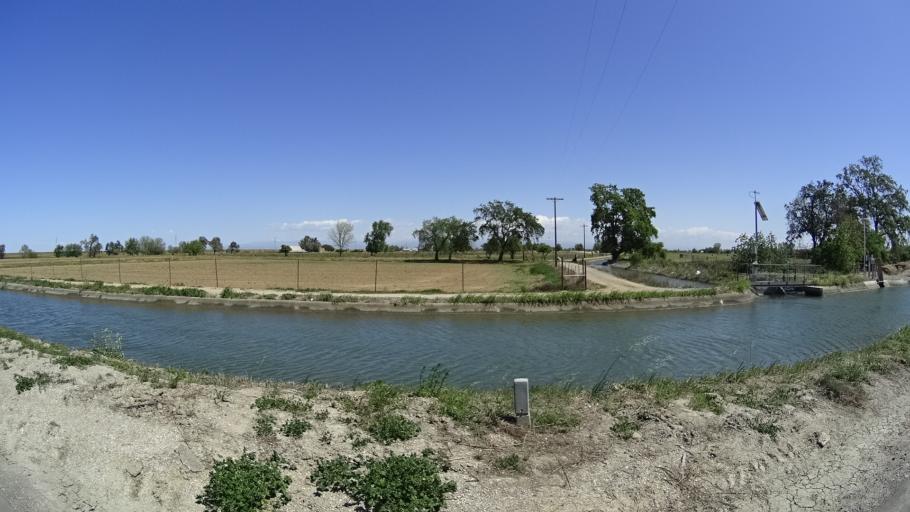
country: US
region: California
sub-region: Glenn County
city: Orland
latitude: 39.7905
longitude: -122.2263
